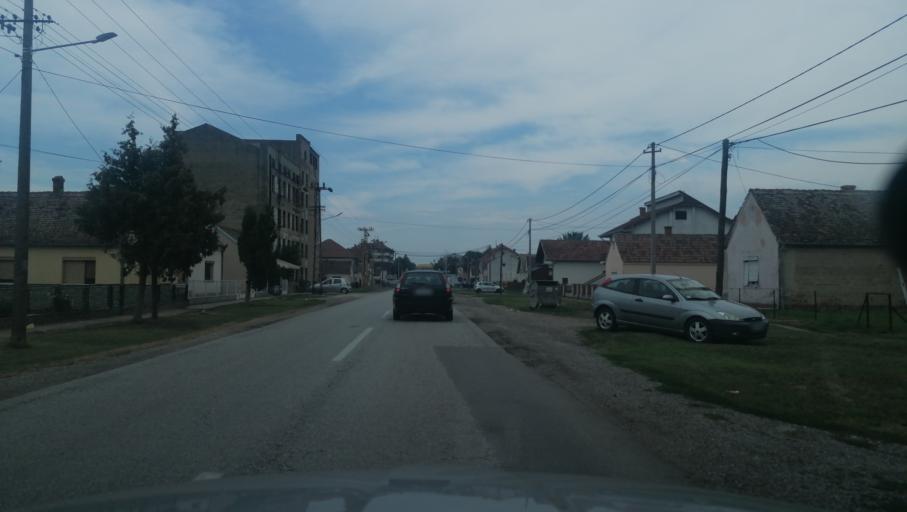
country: RS
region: Central Serbia
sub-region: Macvanski Okrug
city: Bogatic
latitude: 44.8344
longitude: 19.4745
